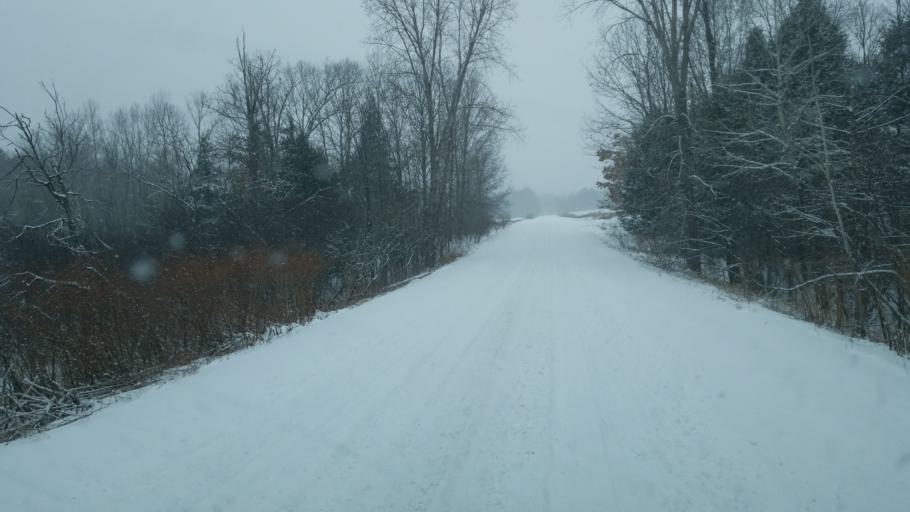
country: US
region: Michigan
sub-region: Mecosta County
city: Canadian Lakes
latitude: 43.5853
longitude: -85.3444
